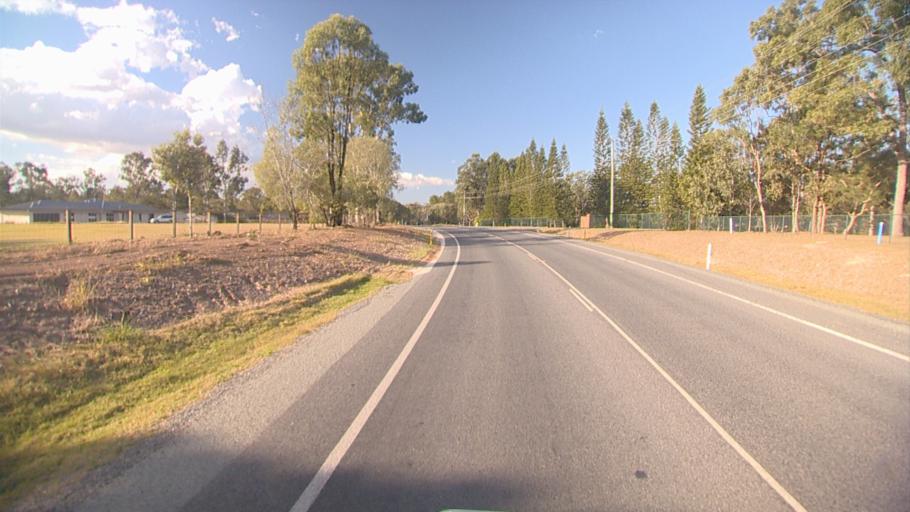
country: AU
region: Queensland
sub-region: Logan
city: Park Ridge South
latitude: -27.7199
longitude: 152.9677
